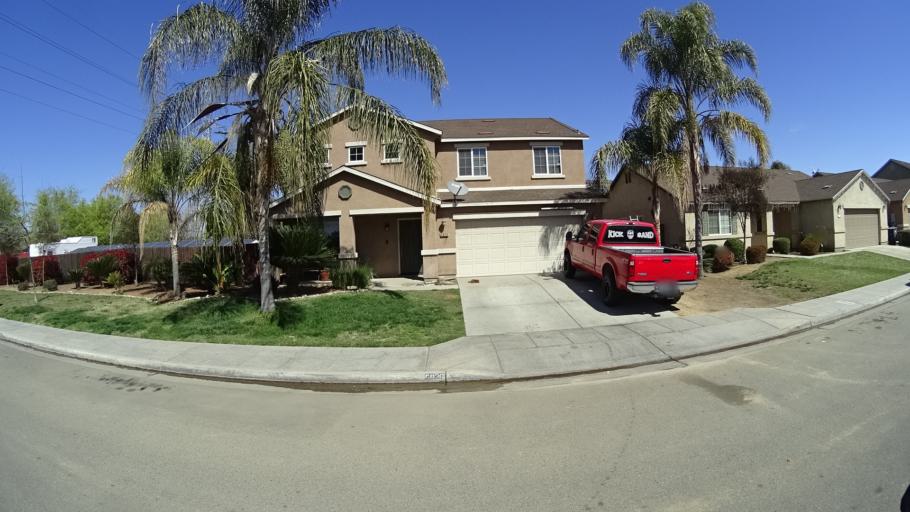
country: US
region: California
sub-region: Fresno County
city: West Park
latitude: 36.7829
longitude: -119.8972
